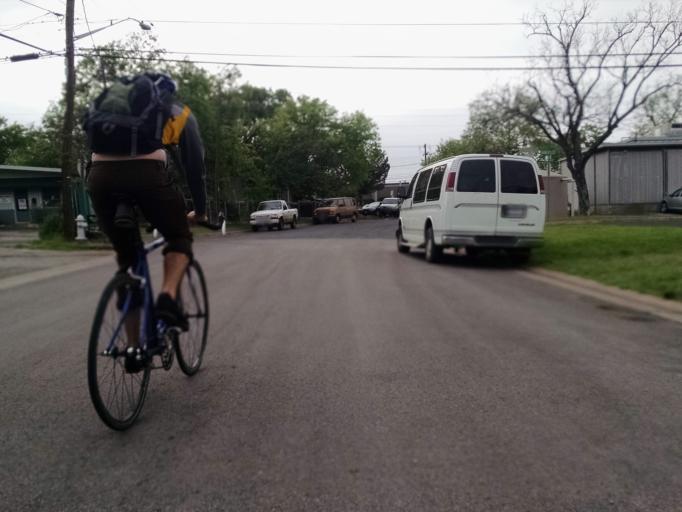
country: US
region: Texas
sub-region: Travis County
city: Austin
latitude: 30.3329
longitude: -97.7204
